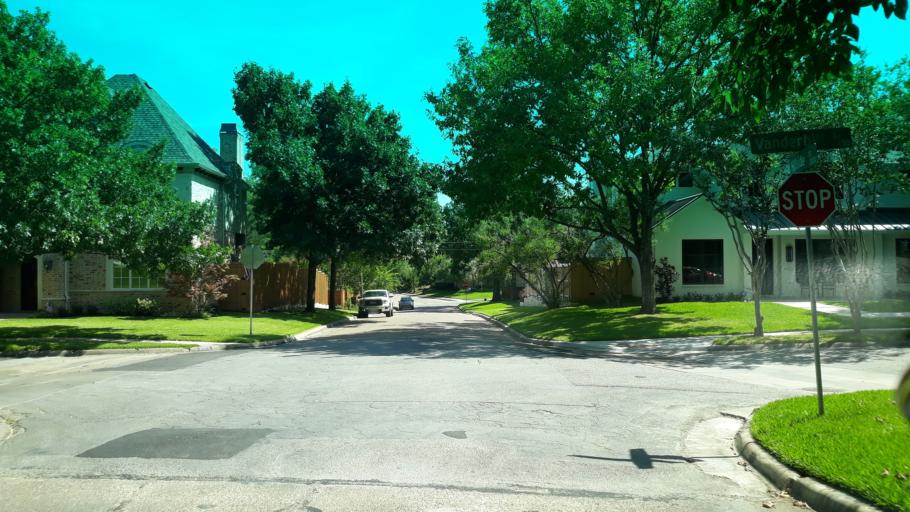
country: US
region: Texas
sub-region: Dallas County
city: Highland Park
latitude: 32.8259
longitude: -96.7501
